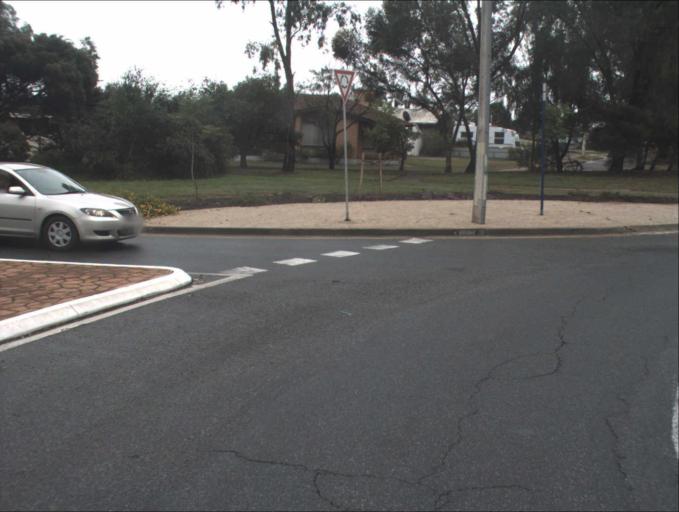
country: AU
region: South Australia
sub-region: Port Adelaide Enfield
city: Gilles Plains
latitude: -34.8351
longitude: 138.6622
